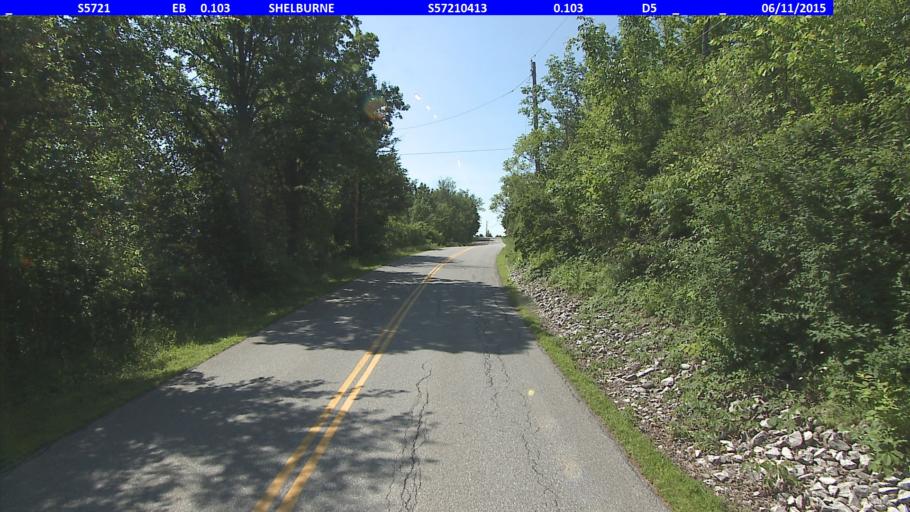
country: US
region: Vermont
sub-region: Chittenden County
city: Burlington
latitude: 44.3692
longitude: -73.2148
